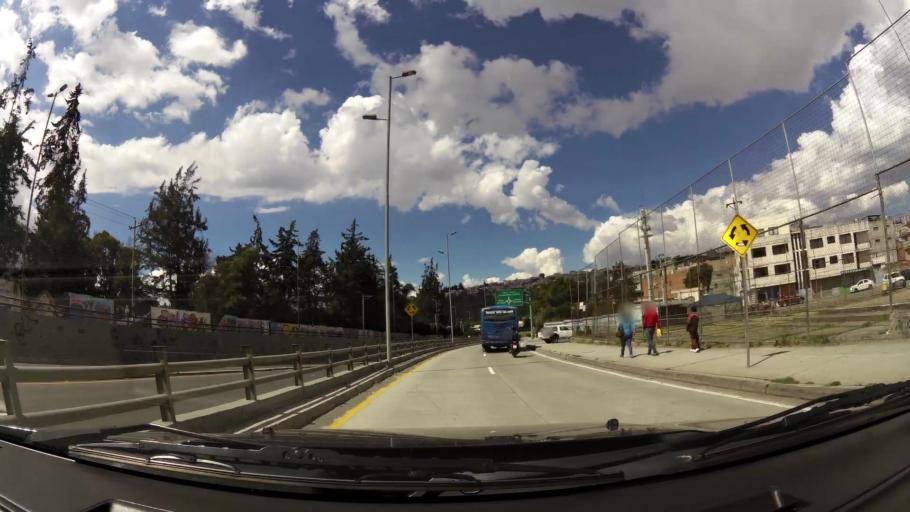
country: EC
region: Pichincha
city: Quito
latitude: -0.1026
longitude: -78.4933
